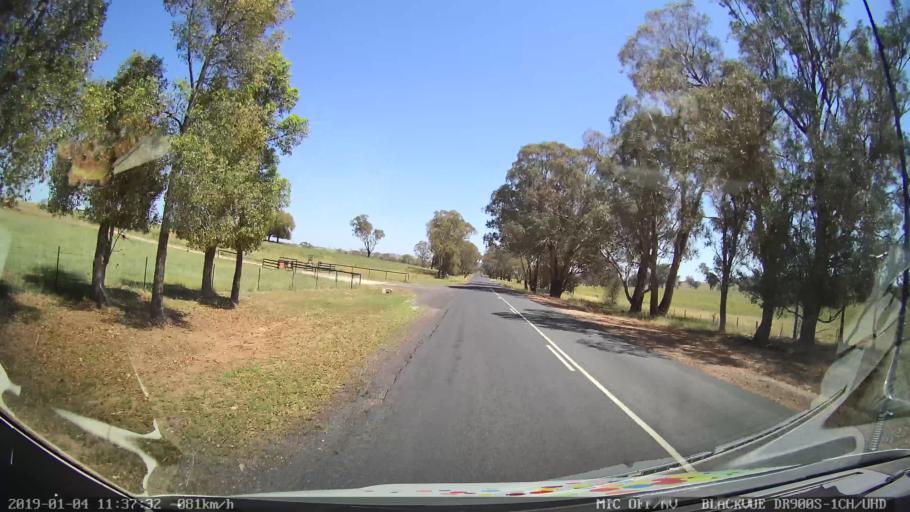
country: AU
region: New South Wales
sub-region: Cabonne
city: Molong
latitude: -33.0313
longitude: 148.8068
